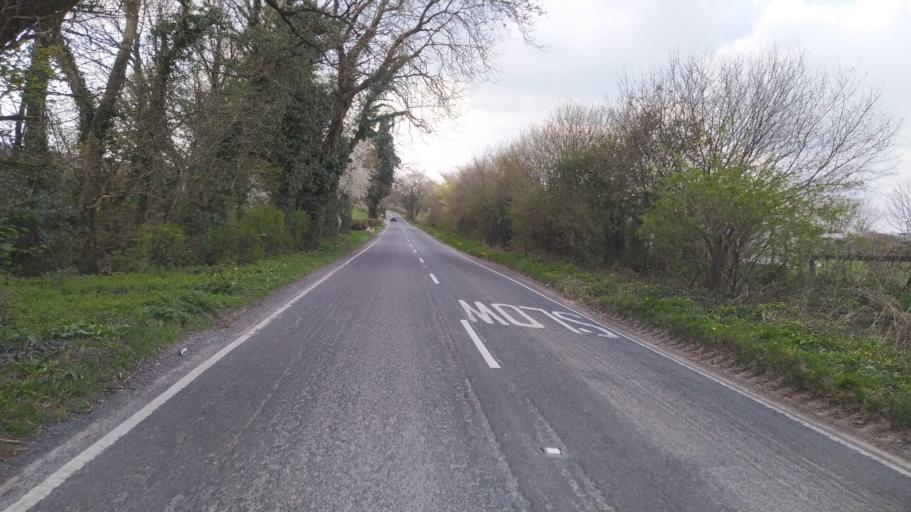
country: GB
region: England
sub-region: Bath and North East Somerset
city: Radstock
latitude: 51.2182
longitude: -2.4335
